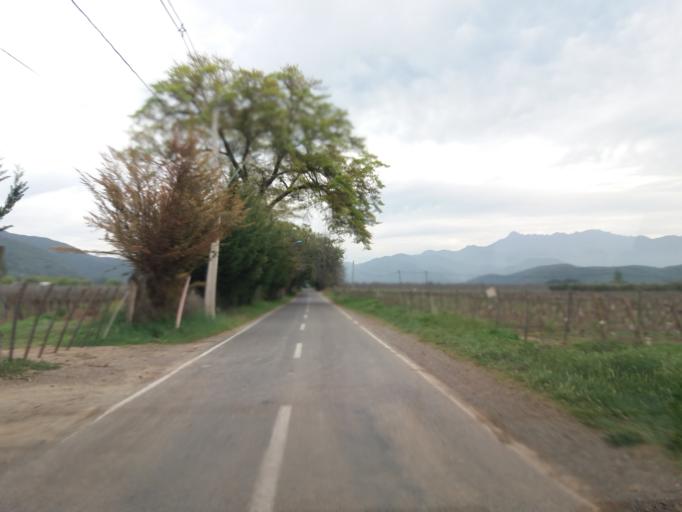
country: CL
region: Valparaiso
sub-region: Provincia de Quillota
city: Quillota
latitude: -32.8994
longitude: -71.1059
